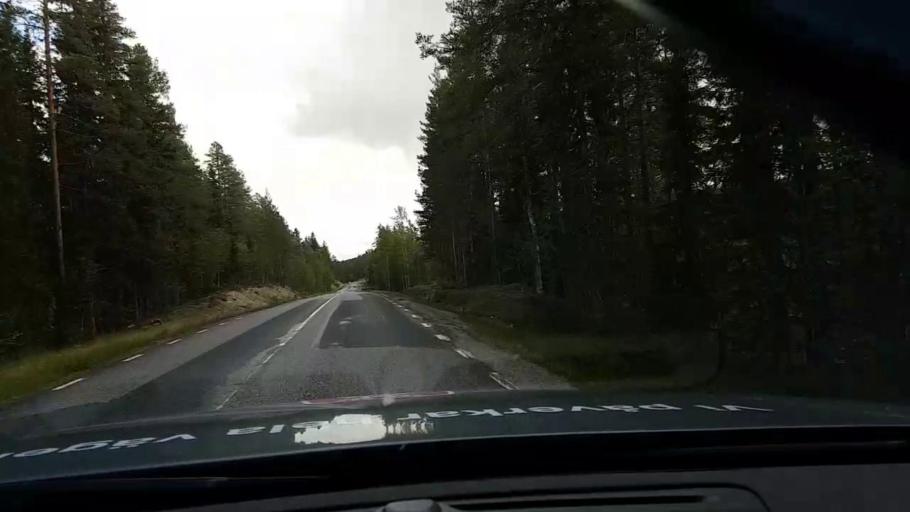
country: SE
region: Vaesterbotten
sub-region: Asele Kommun
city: Asele
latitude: 63.8415
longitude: 17.4270
